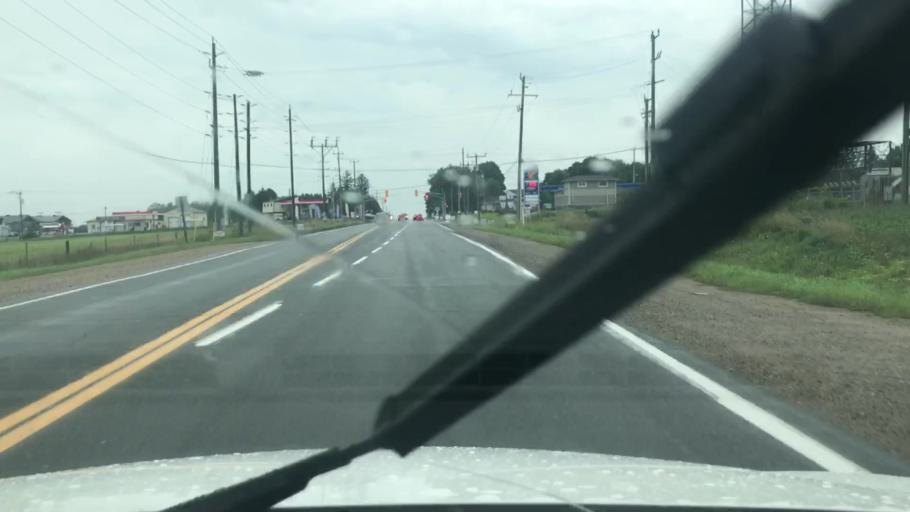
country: CA
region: Ontario
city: Bradford West Gwillimbury
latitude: 44.2144
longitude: -79.5926
